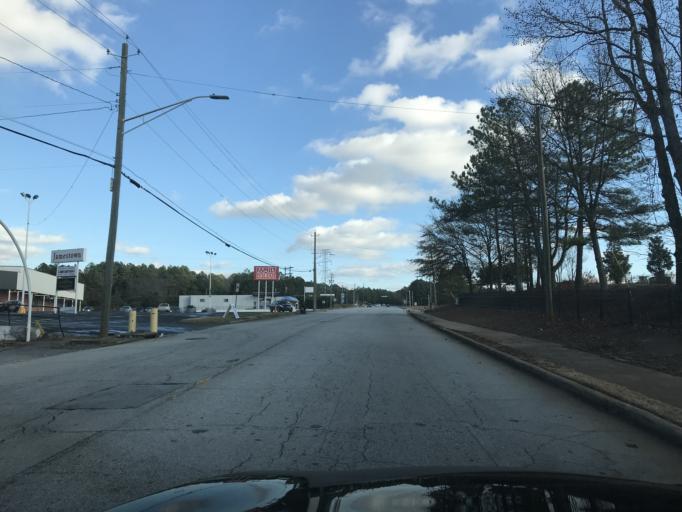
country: US
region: Georgia
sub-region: Fulton County
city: College Park
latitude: 33.6356
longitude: -84.4716
